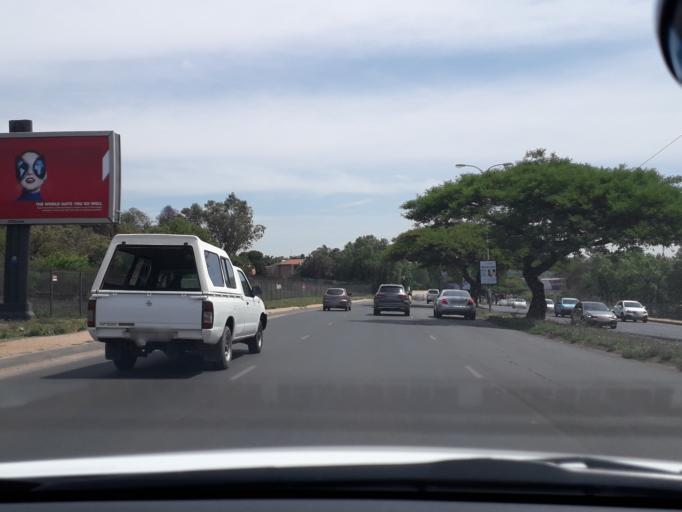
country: ZA
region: Gauteng
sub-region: City of Johannesburg Metropolitan Municipality
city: Johannesburg
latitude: -26.0876
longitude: 28.0245
